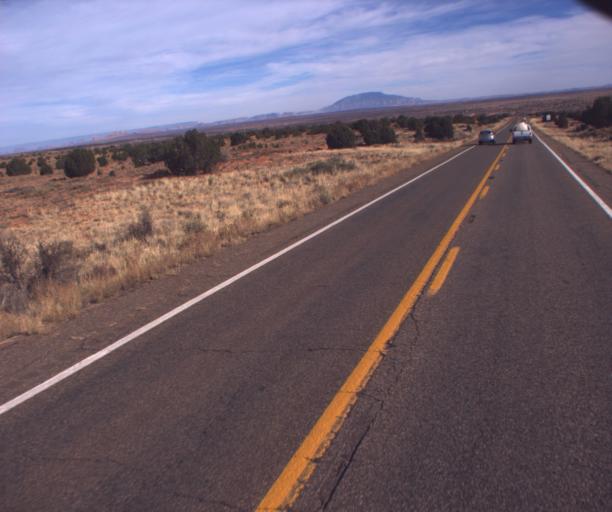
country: US
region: Arizona
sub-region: Coconino County
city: Kaibito
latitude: 36.5913
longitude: -111.0993
